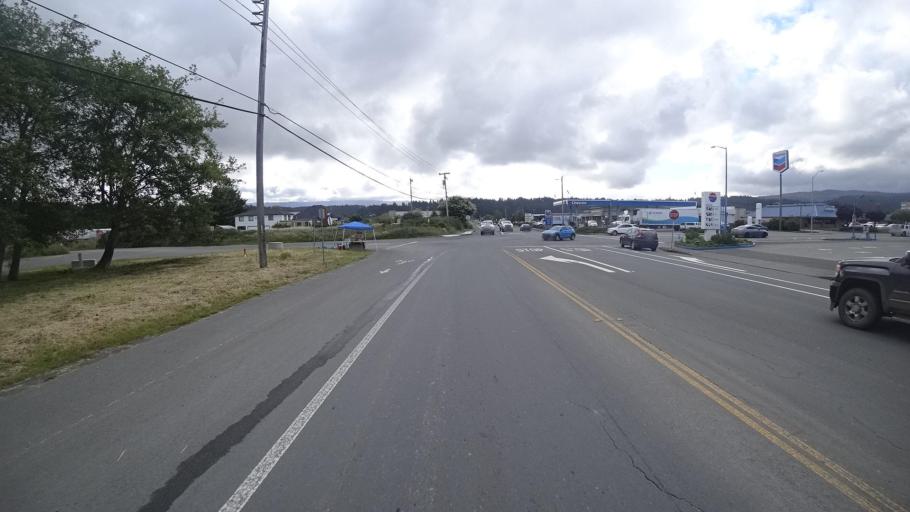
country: US
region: California
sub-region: Humboldt County
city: Arcata
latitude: 40.9051
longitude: -124.0835
